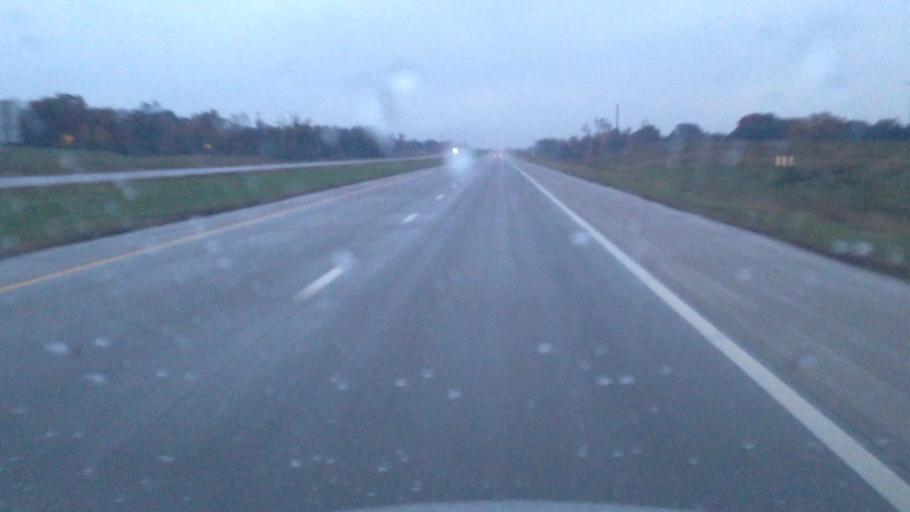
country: US
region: Kansas
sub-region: Douglas County
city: Baldwin City
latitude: 38.7698
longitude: -95.2687
